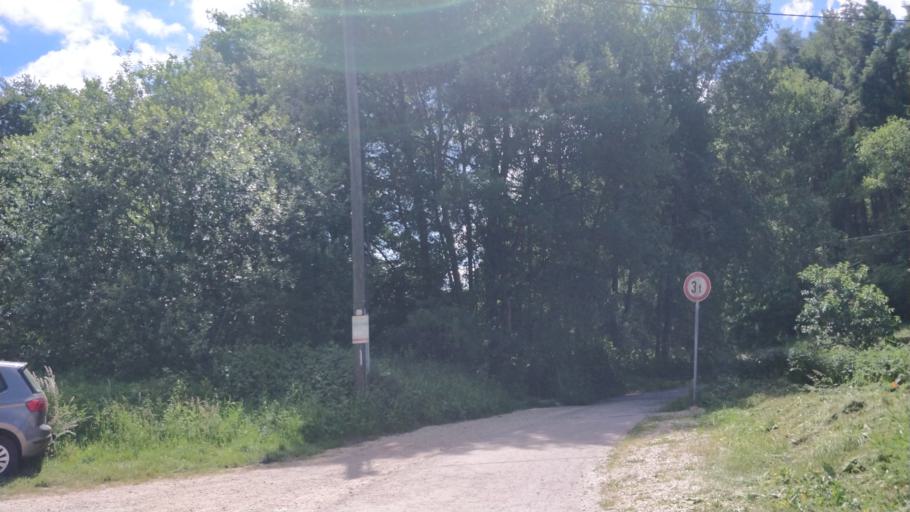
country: DE
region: Rheinland-Pfalz
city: Irsch
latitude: 49.7377
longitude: 6.6684
